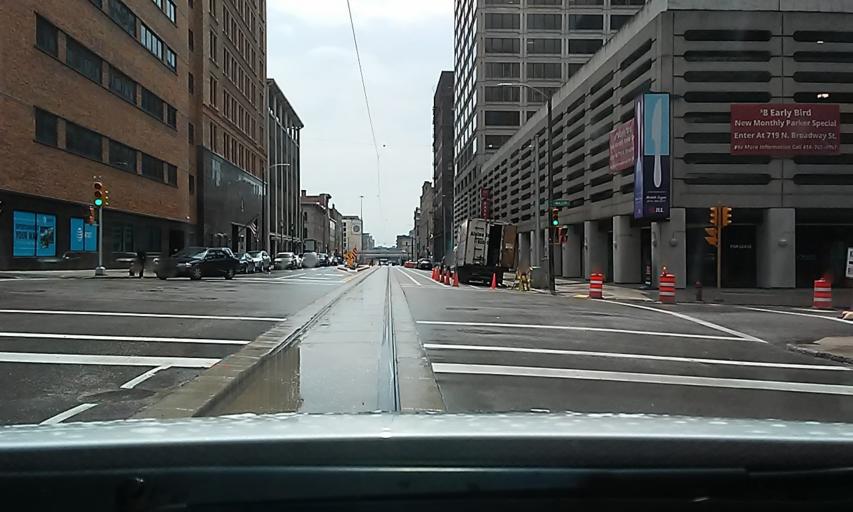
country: US
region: Wisconsin
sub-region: Milwaukee County
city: Milwaukee
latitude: 43.0401
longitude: -87.9080
